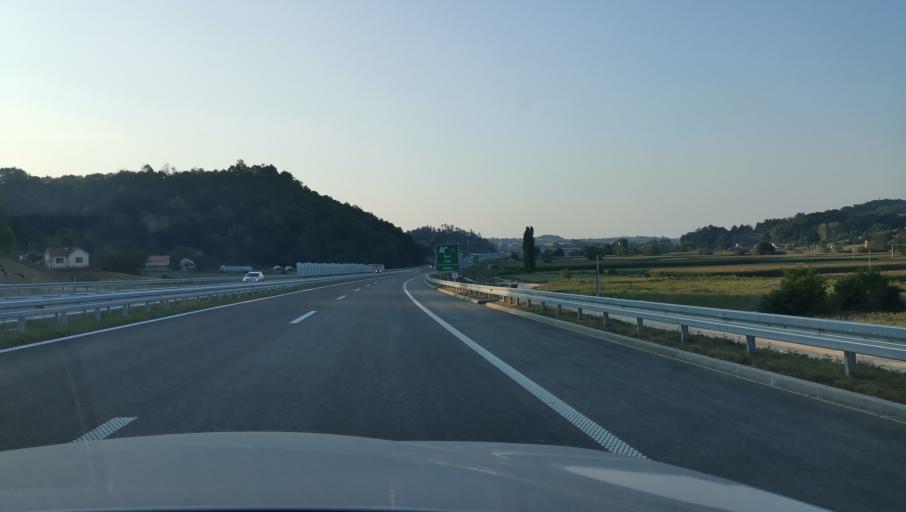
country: RS
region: Central Serbia
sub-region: Kolubarski Okrug
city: Ljig
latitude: 44.2183
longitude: 20.2573
